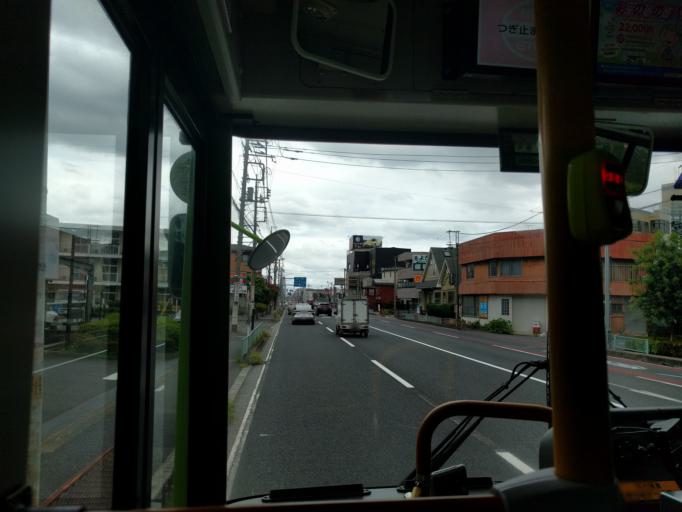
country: JP
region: Saitama
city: Kawaguchi
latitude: 35.8048
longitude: 139.7330
